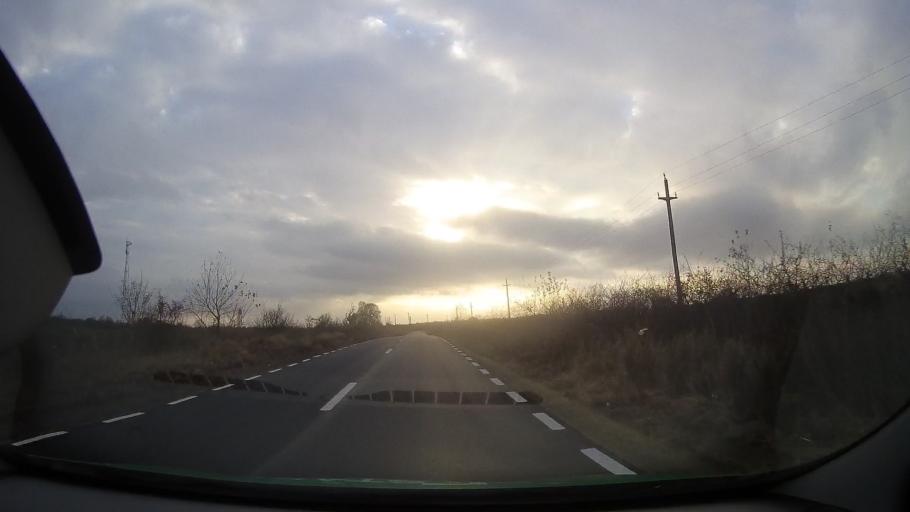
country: RO
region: Constanta
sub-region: Comuna Adamclisi
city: Adamclisi
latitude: 44.0692
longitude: 27.9790
